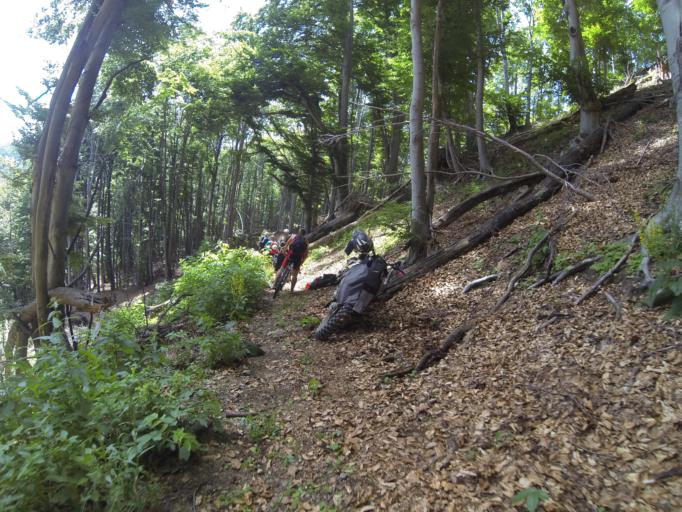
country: RO
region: Valcea
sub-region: Oras Baile Olanesti
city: Cheia
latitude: 45.2290
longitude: 24.1855
